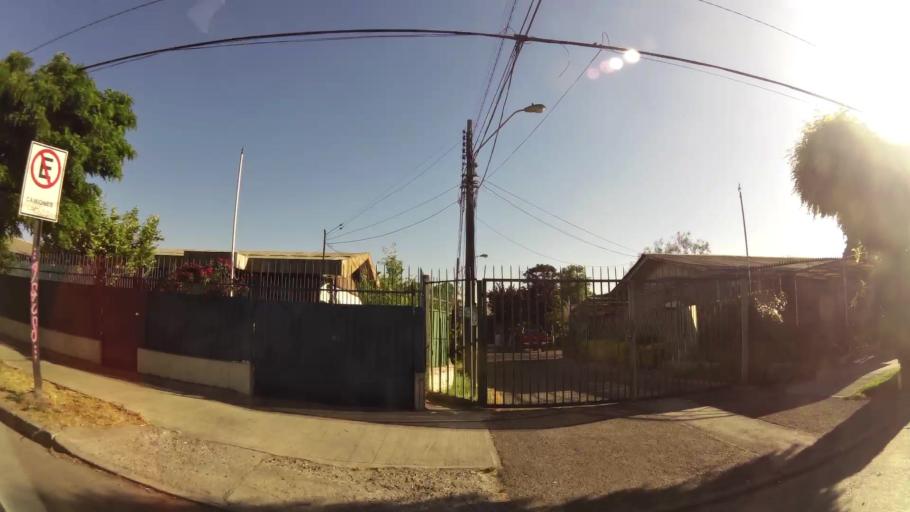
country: CL
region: Santiago Metropolitan
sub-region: Provincia de Santiago
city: La Pintana
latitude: -33.5450
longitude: -70.6723
